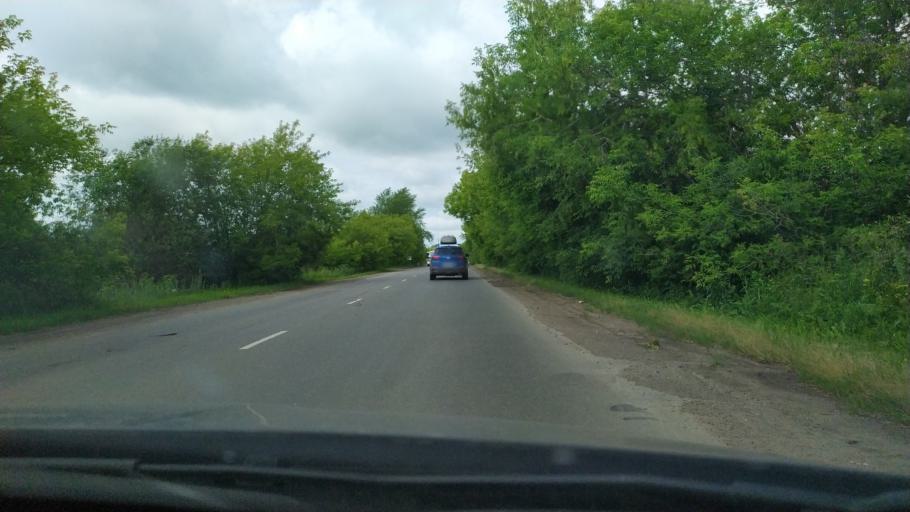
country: RU
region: Perm
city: Kondratovo
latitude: 57.9282
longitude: 56.1114
